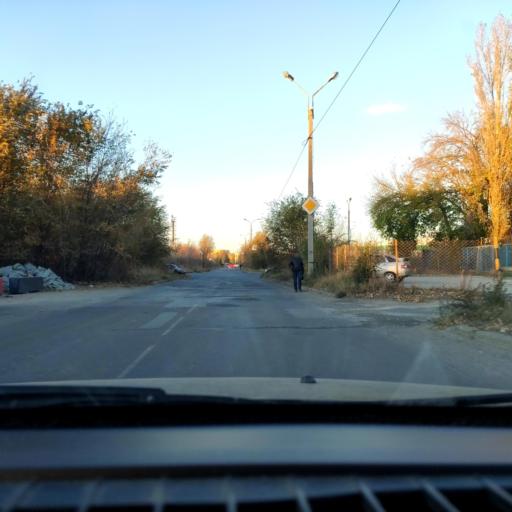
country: RU
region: Samara
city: Tol'yatti
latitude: 53.5543
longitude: 49.3139
